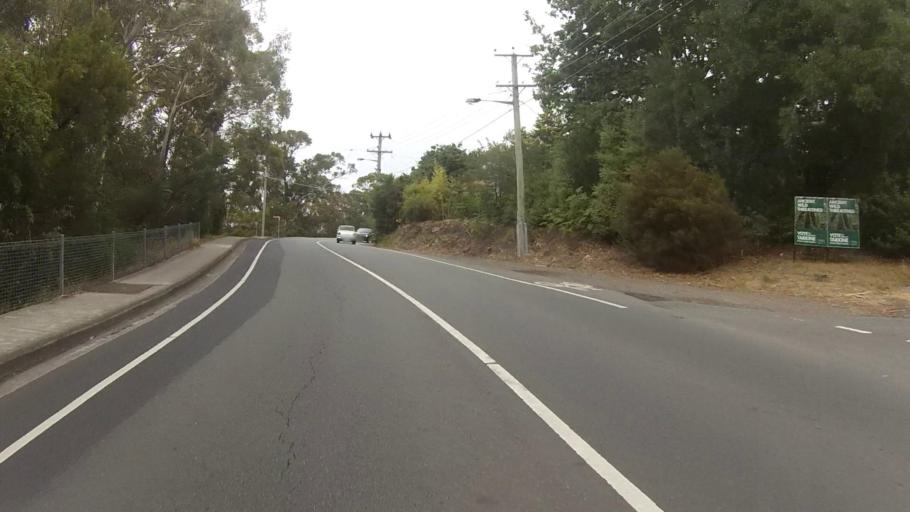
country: AU
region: Tasmania
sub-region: Kingborough
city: Taroona
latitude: -42.9392
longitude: 147.3529
